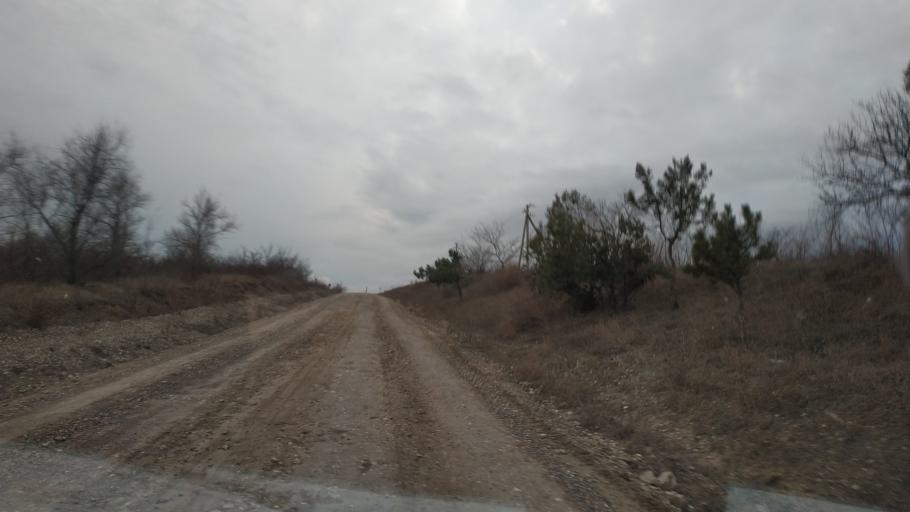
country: MD
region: Causeni
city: Causeni
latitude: 46.6260
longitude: 29.3965
